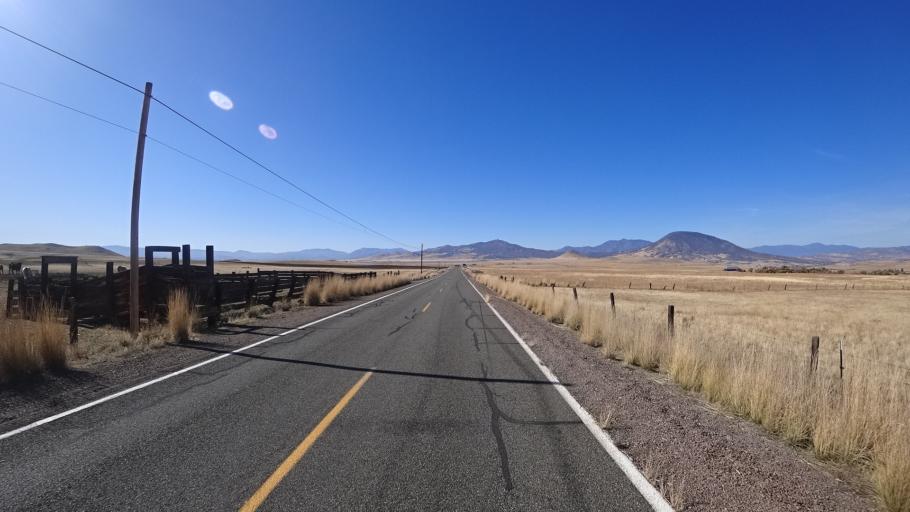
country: US
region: California
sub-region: Siskiyou County
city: Montague
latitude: 41.8044
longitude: -122.4050
